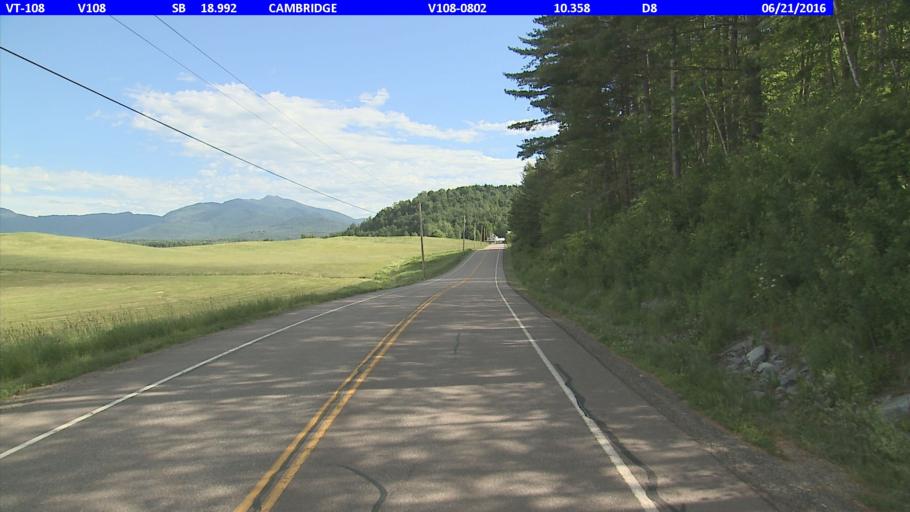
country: US
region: Vermont
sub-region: Lamoille County
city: Johnson
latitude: 44.6652
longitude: -72.8292
